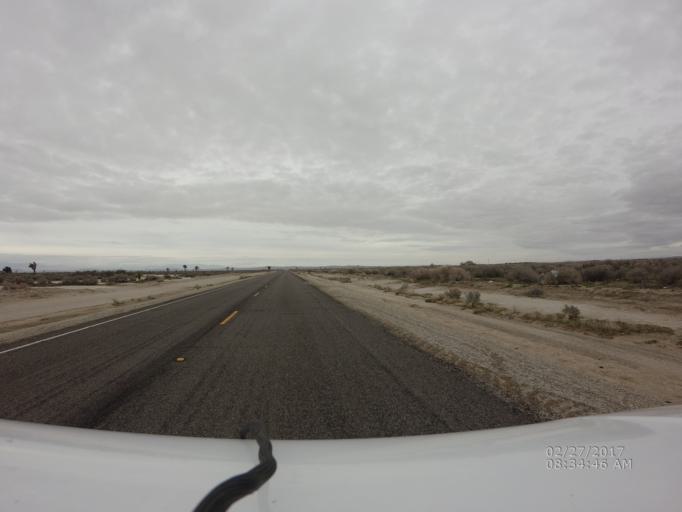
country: US
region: California
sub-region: Los Angeles County
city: Lancaster
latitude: 34.7154
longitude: -118.0592
